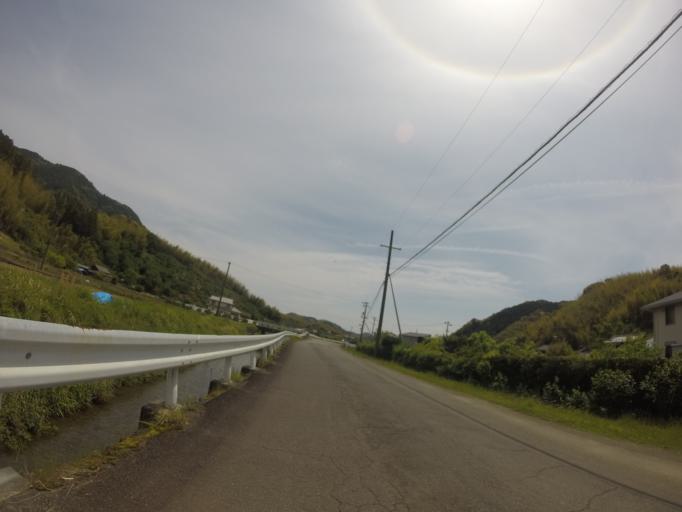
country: JP
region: Shizuoka
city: Fujieda
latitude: 34.9289
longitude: 138.2327
